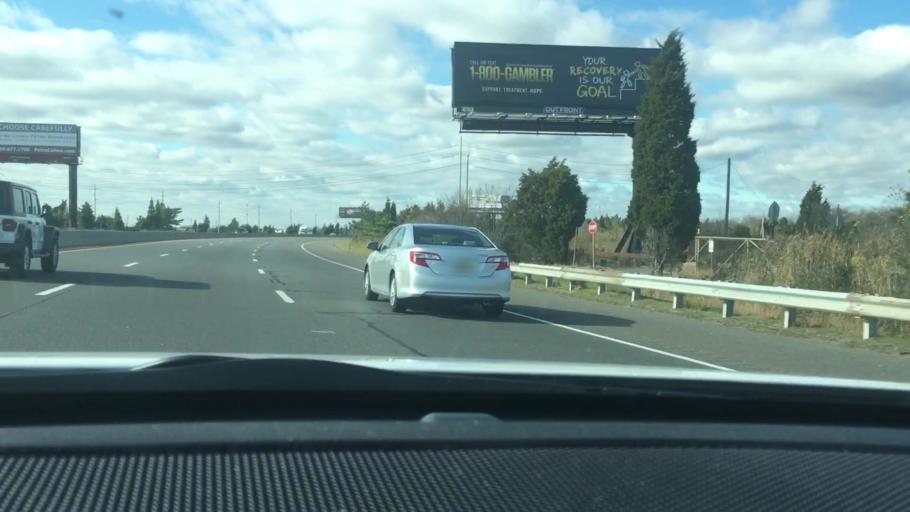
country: US
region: New Jersey
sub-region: Atlantic County
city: Ventnor City
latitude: 39.3676
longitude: -74.4604
